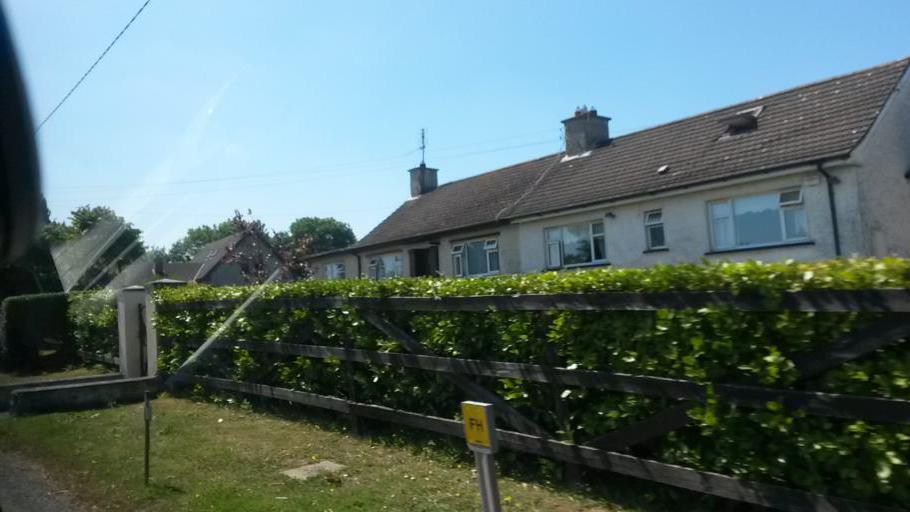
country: IE
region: Leinster
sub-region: An Mhi
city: Stamullin
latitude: 53.5826
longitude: -6.3038
